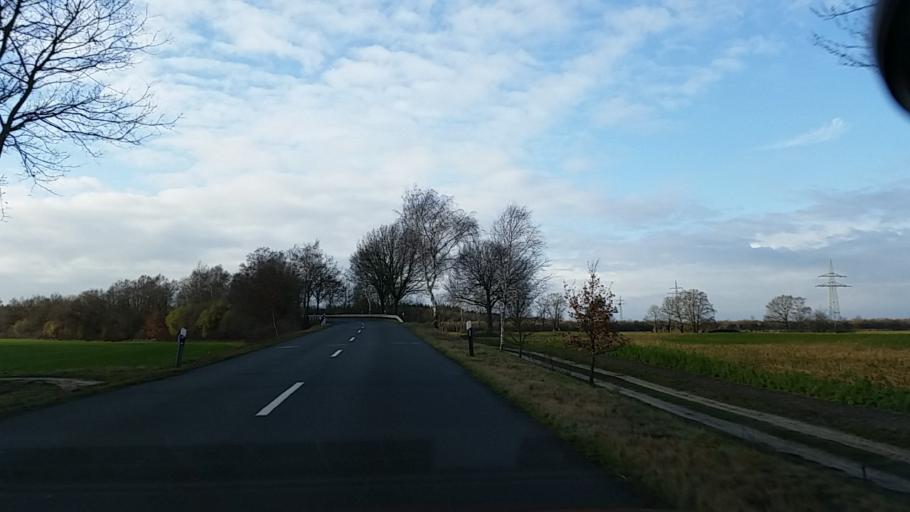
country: DE
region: Lower Saxony
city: Wieren
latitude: 52.8870
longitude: 10.6368
